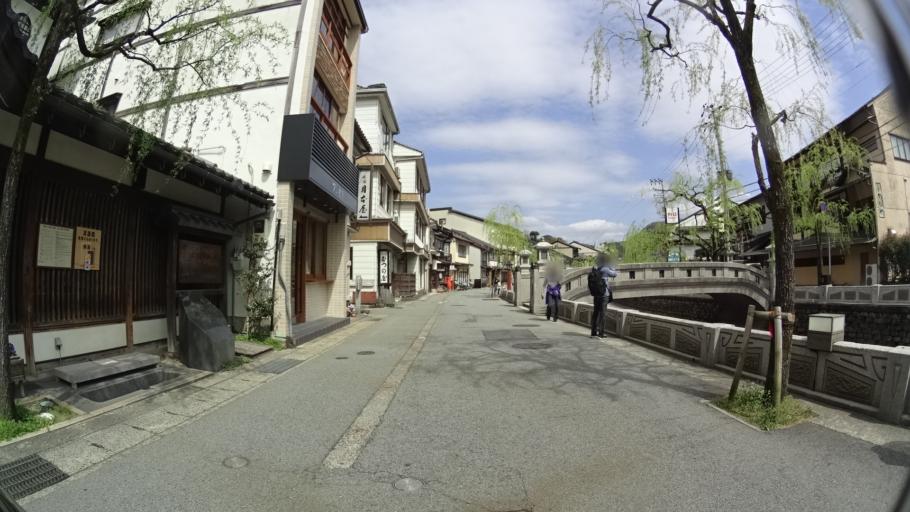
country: JP
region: Hyogo
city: Toyooka
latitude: 35.6223
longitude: 134.8086
